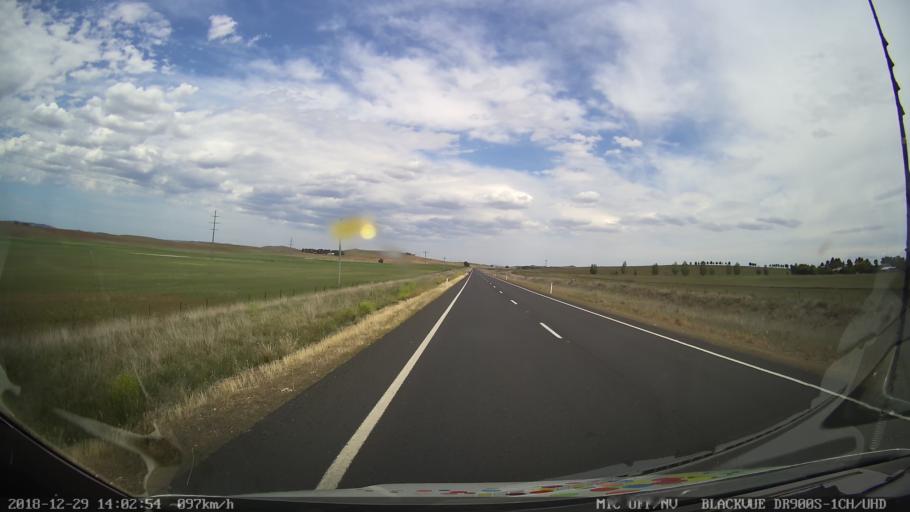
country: AU
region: New South Wales
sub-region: Cooma-Monaro
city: Cooma
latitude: -36.2940
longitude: 149.1804
